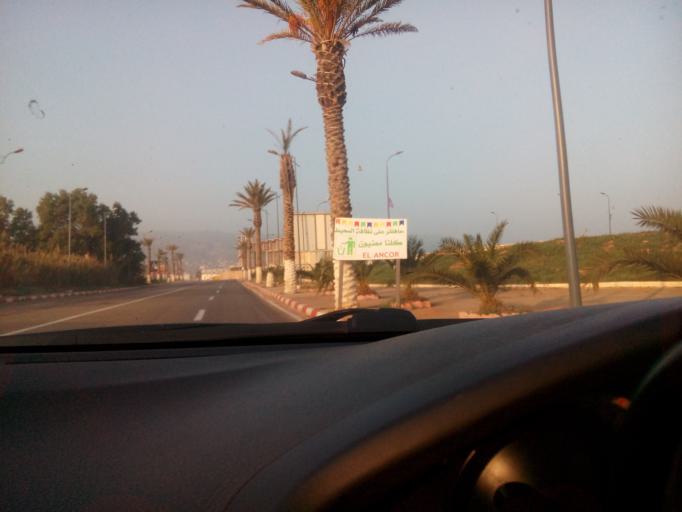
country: DZ
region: Oran
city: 'Ain el Turk
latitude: 35.7073
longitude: -0.8806
